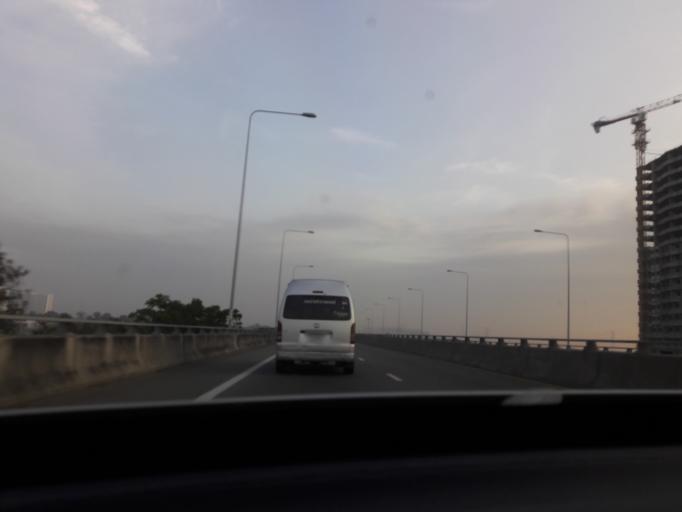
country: TH
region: Bangkok
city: Don Mueang
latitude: 13.9220
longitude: 100.5488
